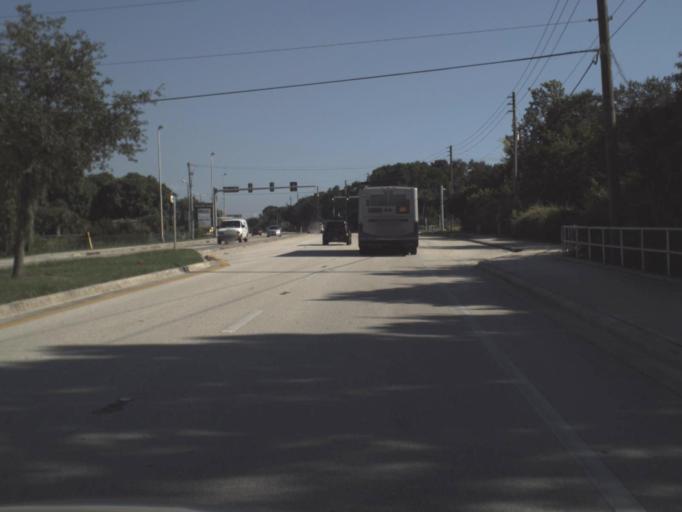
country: US
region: Florida
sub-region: Sarasota County
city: Englewood
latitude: 27.0015
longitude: -82.3775
